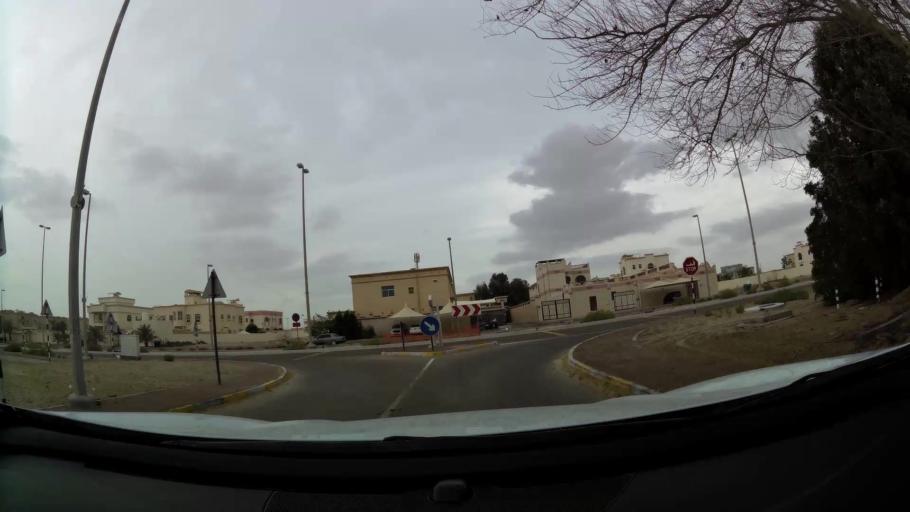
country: AE
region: Abu Dhabi
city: Abu Dhabi
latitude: 24.3741
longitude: 54.6431
